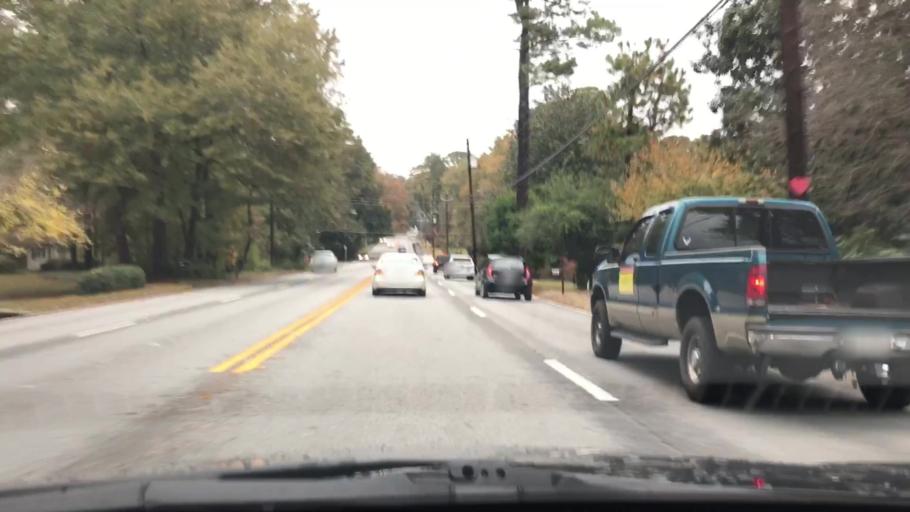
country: US
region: Georgia
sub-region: DeKalb County
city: North Druid Hills
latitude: 33.8145
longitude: -84.3069
